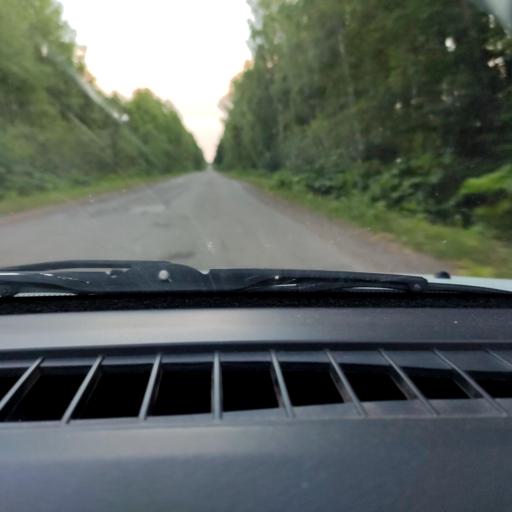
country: RU
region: Perm
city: Orda
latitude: 57.2645
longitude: 56.5339
